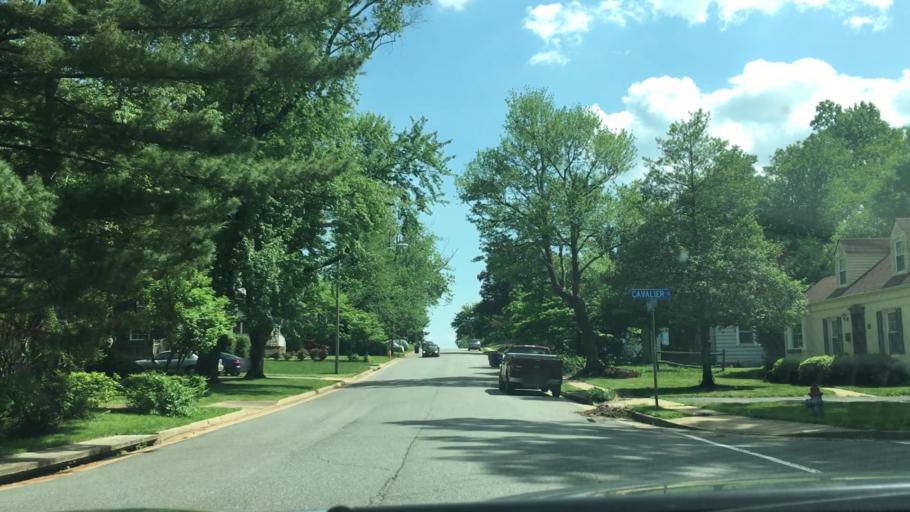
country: US
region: Virginia
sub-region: City of Falls Church
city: Falls Church
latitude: 38.8781
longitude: -77.1805
